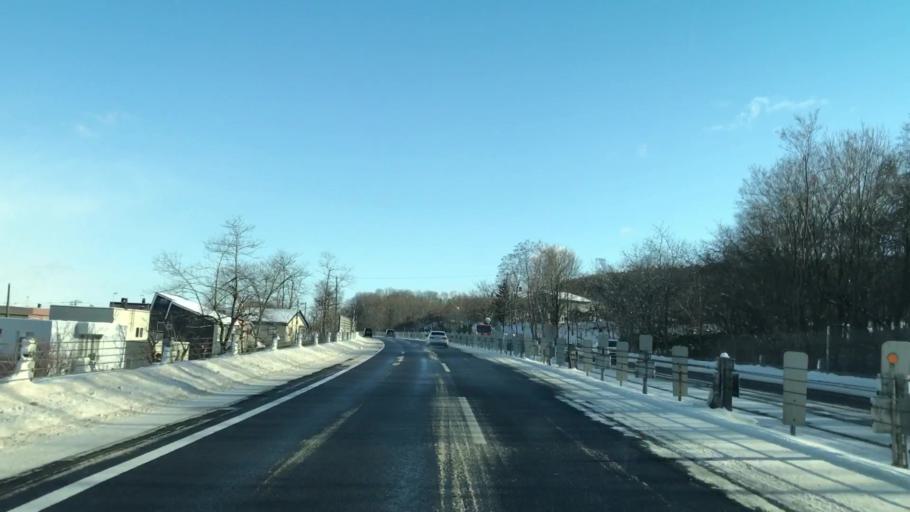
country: JP
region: Hokkaido
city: Sapporo
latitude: 43.1199
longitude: 141.2211
